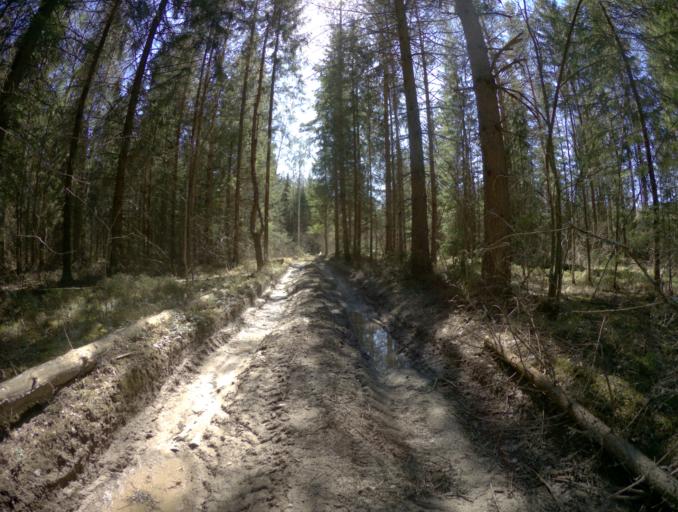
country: RU
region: Vladimir
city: Ivanishchi
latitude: 55.8329
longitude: 40.4329
